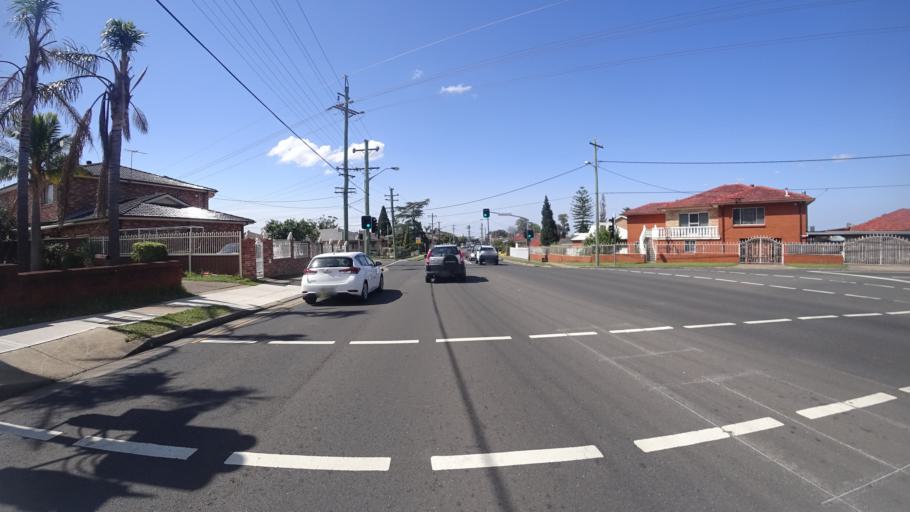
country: AU
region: New South Wales
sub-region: Fairfield
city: Liverpool
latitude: -33.8981
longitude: 150.9249
